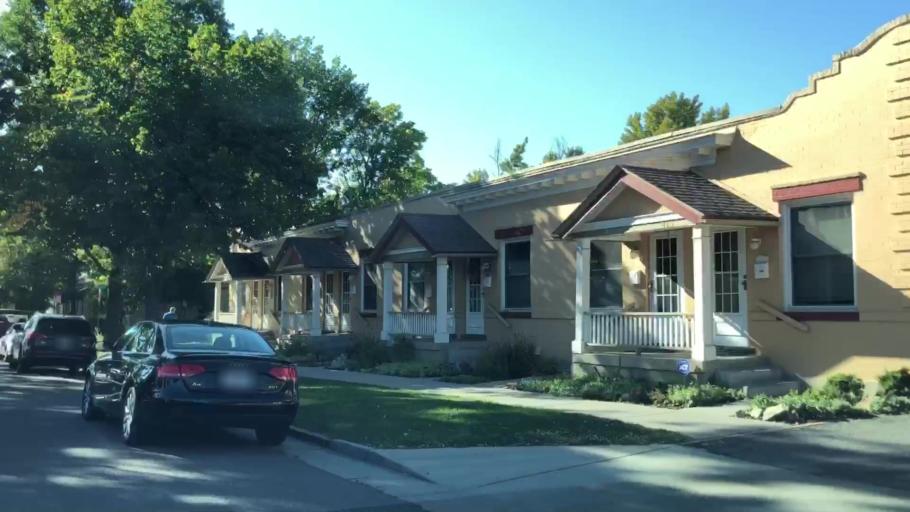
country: US
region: Colorado
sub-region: Denver County
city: Denver
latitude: 39.7040
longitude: -104.9846
